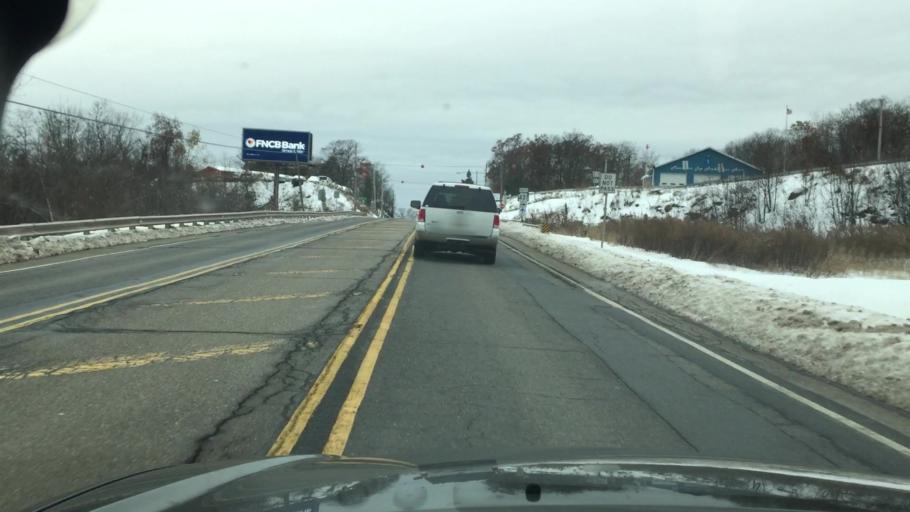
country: US
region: Pennsylvania
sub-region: Luzerne County
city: Mountain Top
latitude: 41.1740
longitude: -75.8799
